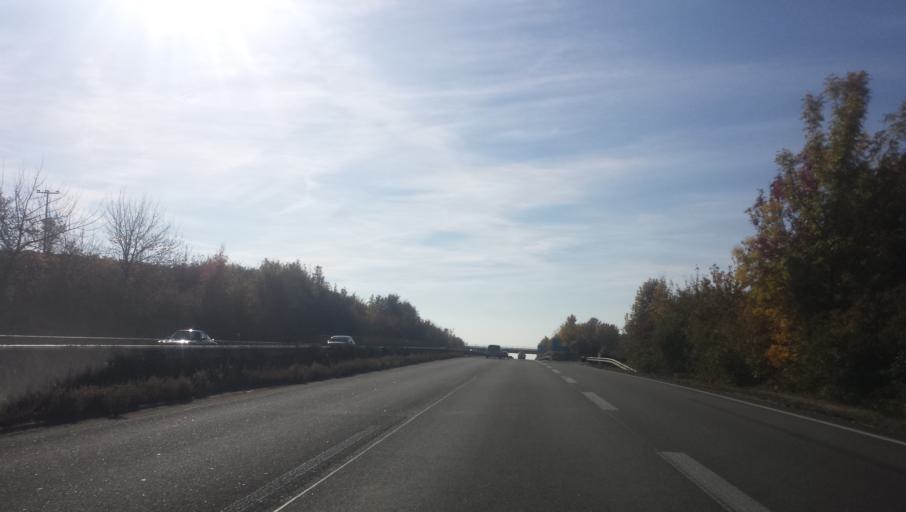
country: DE
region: Rheinland-Pfalz
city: Kirrweiler
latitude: 49.2902
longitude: 8.1524
